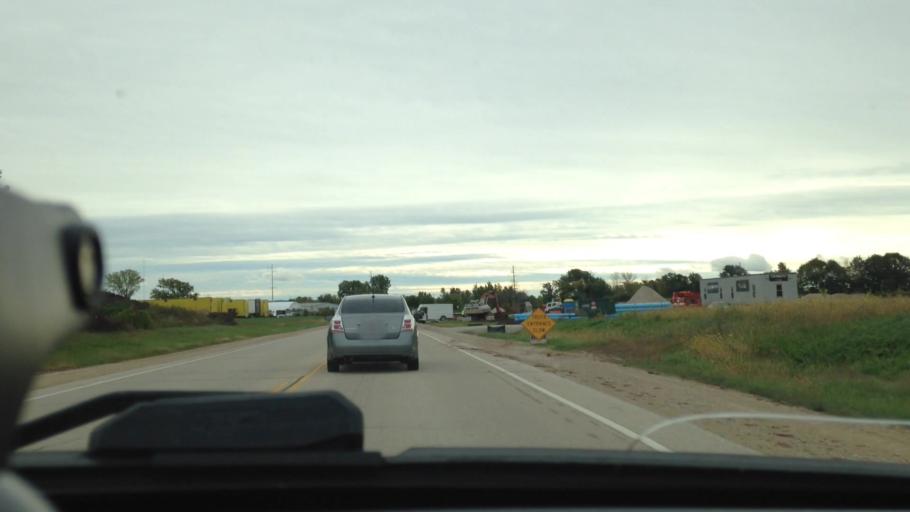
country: US
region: Wisconsin
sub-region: Fond du Lac County
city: North Fond du Lac
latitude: 43.7982
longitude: -88.4910
